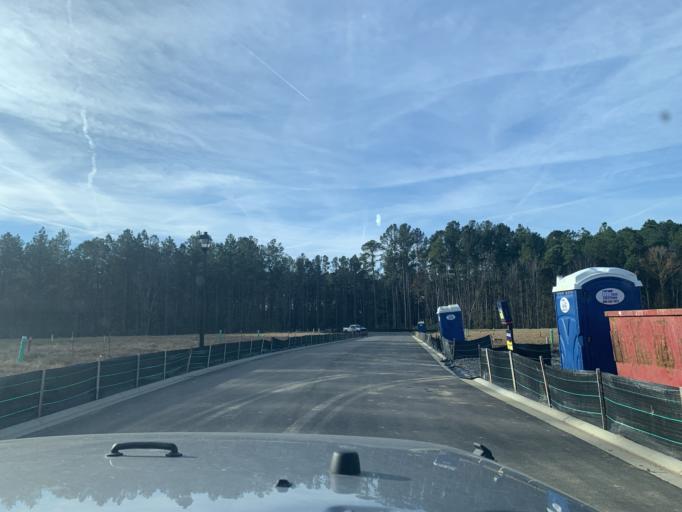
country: US
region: Georgia
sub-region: Chatham County
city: Pooler
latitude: 32.0662
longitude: -81.2566
